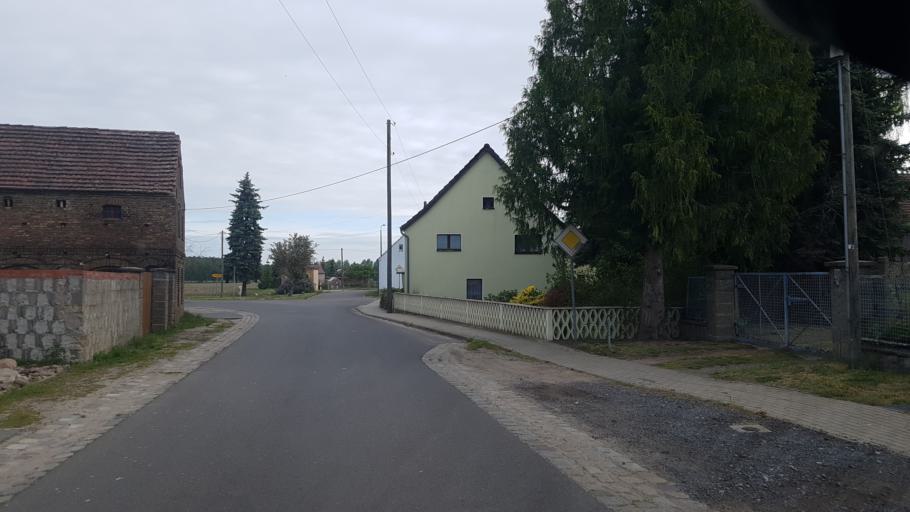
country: DE
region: Brandenburg
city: Luckenwalde
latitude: 52.1126
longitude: 13.1110
